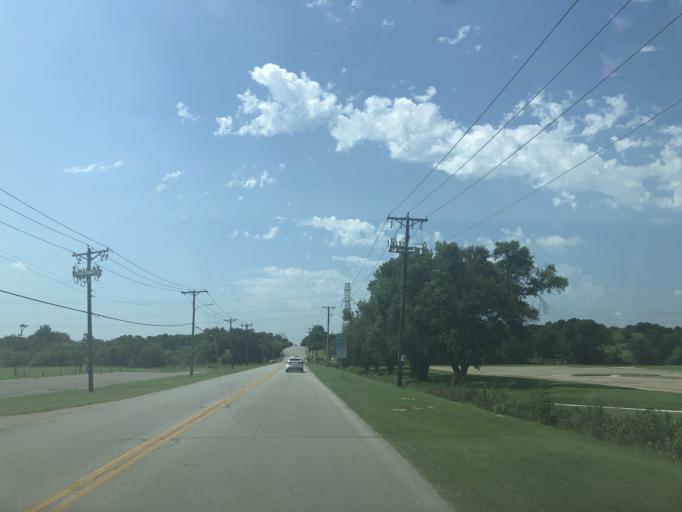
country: US
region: Texas
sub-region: Dallas County
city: Grand Prairie
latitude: 32.7277
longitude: -97.0072
